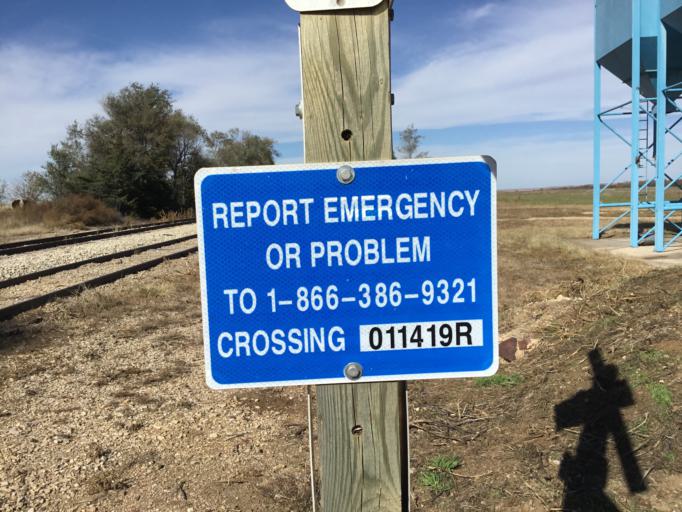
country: US
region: Kansas
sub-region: Lincoln County
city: Lincoln
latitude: 38.9304
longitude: -98.0115
